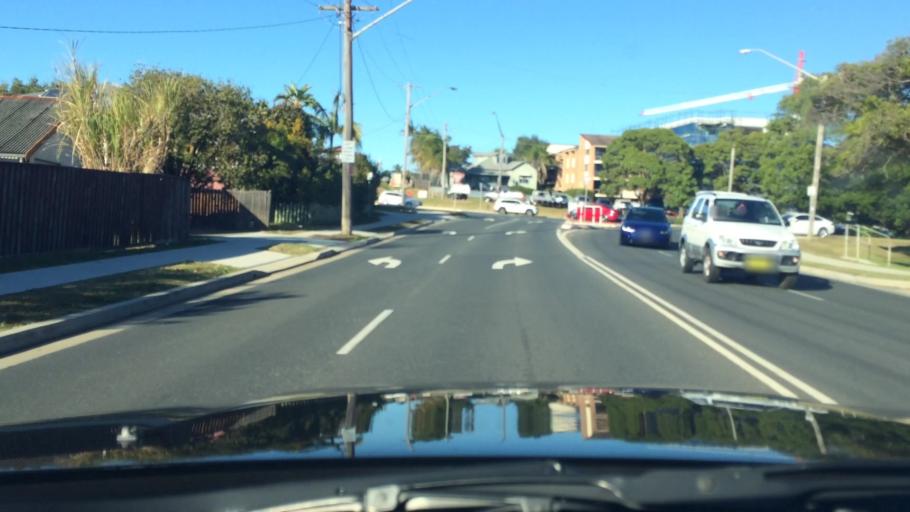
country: AU
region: New South Wales
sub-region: Port Macquarie-Hastings
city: Port Macquarie
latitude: -31.4328
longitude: 152.8994
